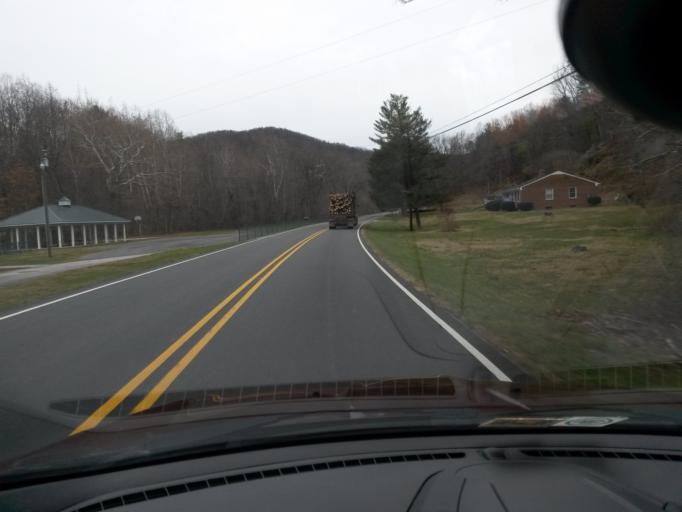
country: US
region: Virginia
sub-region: City of Buena Vista
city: Buena Vista
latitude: 37.6680
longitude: -79.2106
